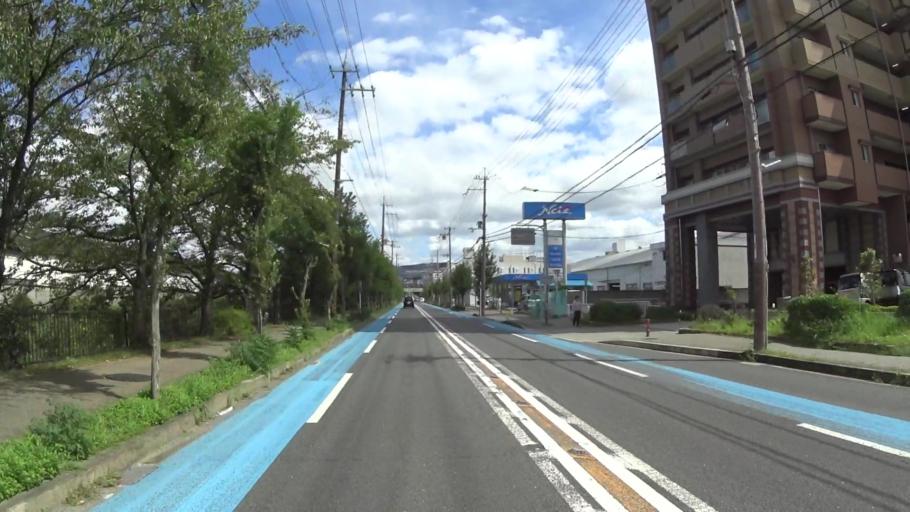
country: JP
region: Kyoto
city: Uji
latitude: 34.8742
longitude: 135.7663
